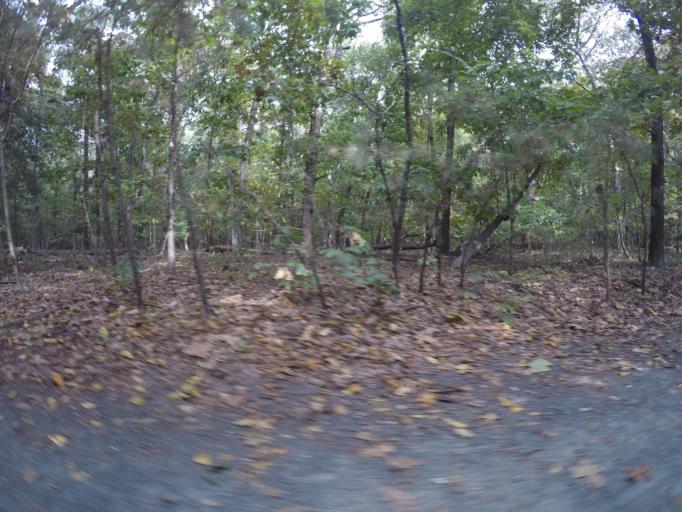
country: US
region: Delaware
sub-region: Sussex County
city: Rehoboth Beach
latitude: 38.7170
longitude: -75.1042
